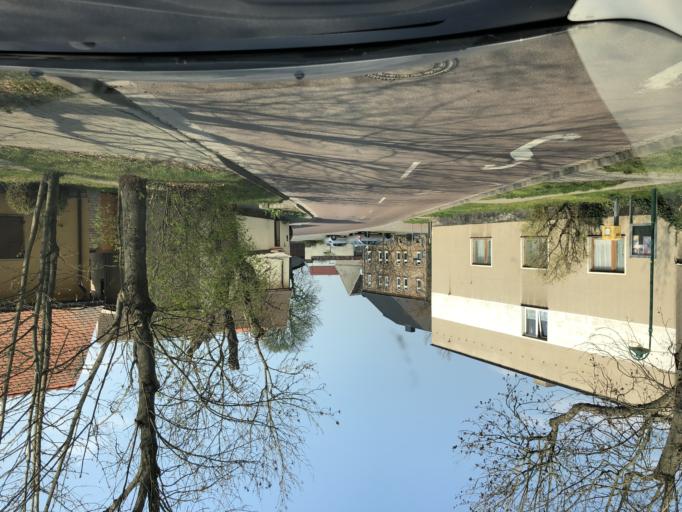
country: DE
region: Saxony-Anhalt
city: Niemberg
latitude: 51.5646
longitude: 12.1331
